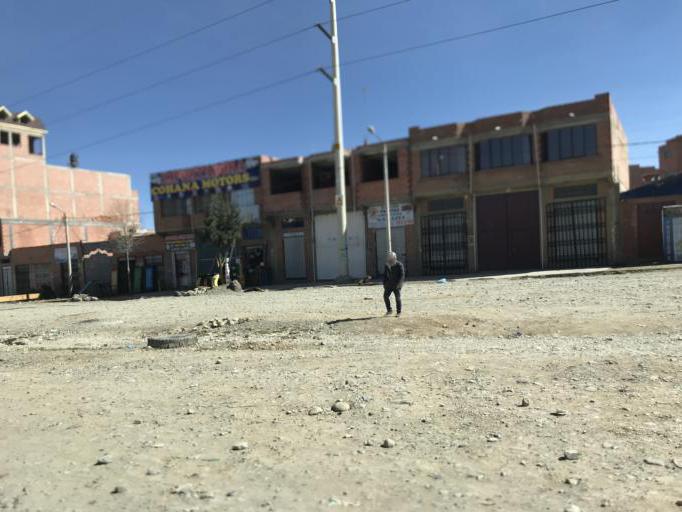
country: BO
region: La Paz
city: La Paz
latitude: -16.4992
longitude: -68.2334
